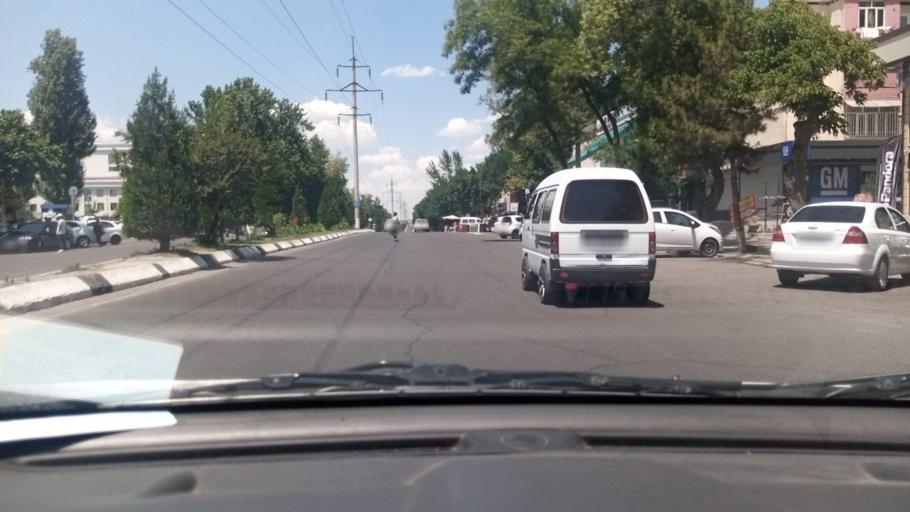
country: UZ
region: Toshkent Shahri
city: Tashkent
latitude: 41.2838
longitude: 69.1947
